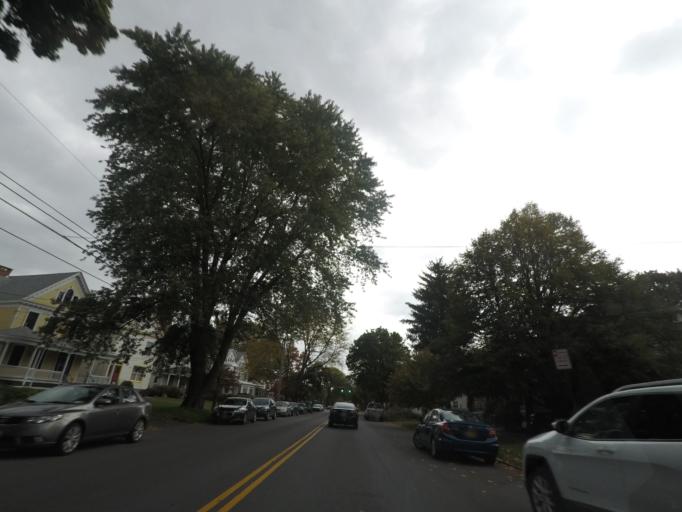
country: US
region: New York
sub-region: Albany County
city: West Albany
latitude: 42.6657
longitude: -73.7894
